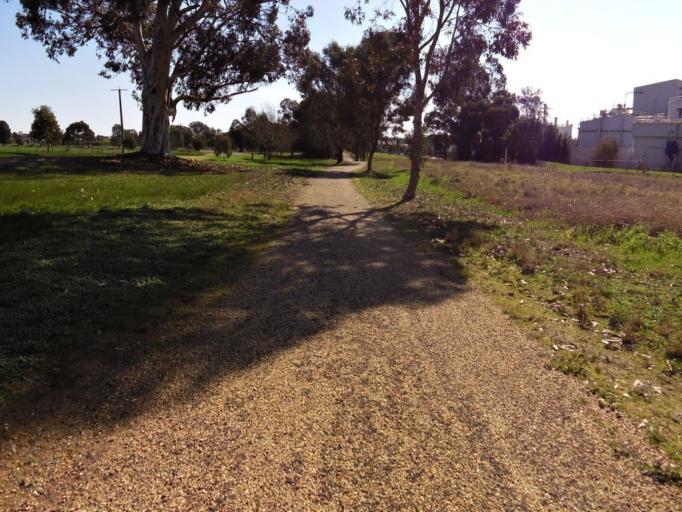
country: AU
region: New South Wales
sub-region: Corowa Shire
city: Corowa
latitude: -36.0143
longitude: 146.4107
